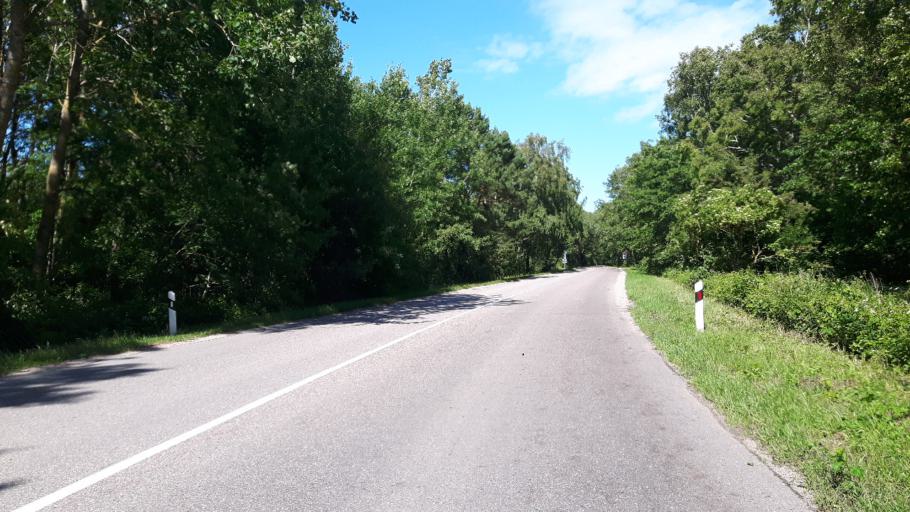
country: RU
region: Kaliningrad
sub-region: Zelenogradskiy Rayon
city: Zelenogradsk
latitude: 55.0259
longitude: 20.6279
